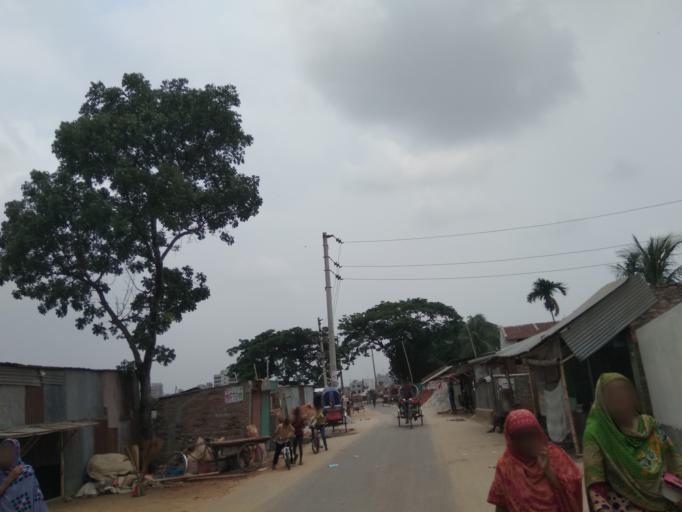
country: BD
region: Dhaka
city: Tungi
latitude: 23.8177
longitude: 90.3823
